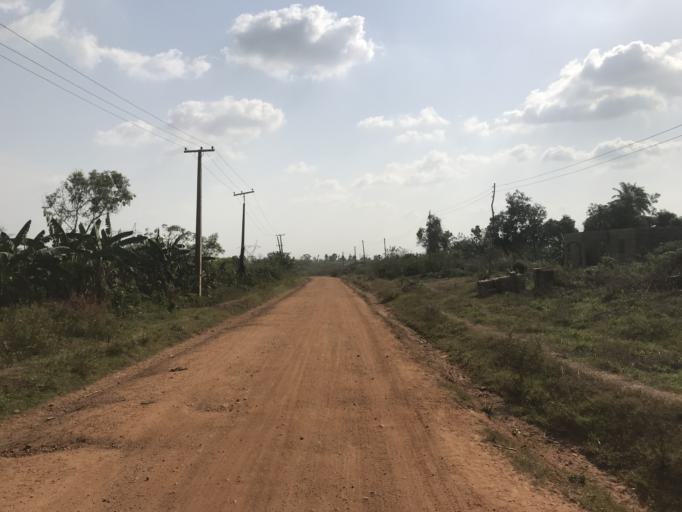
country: NG
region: Osun
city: Osogbo
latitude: 7.8369
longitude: 4.5715
